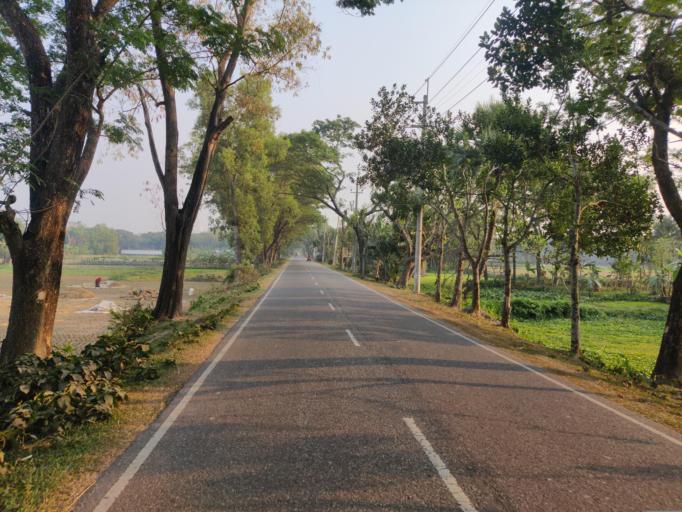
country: BD
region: Dhaka
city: Narsingdi
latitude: 24.0897
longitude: 90.7264
